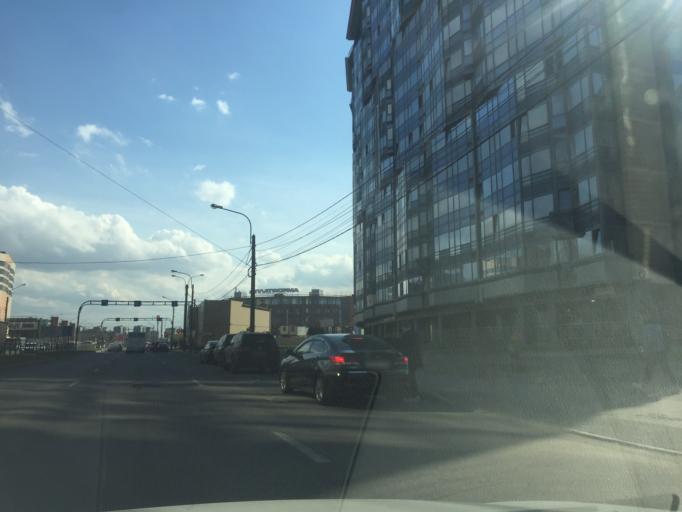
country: RU
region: St.-Petersburg
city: Krasnogvargeisky
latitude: 59.9351
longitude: 30.4352
